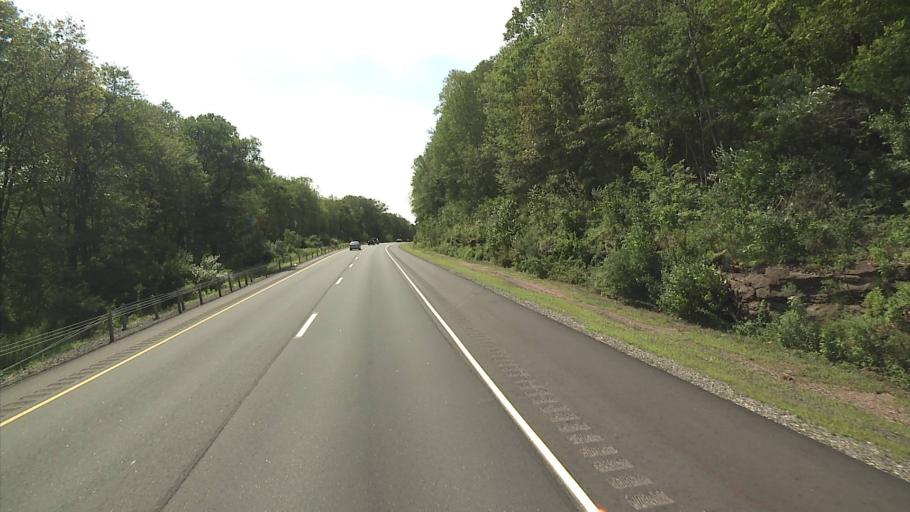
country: US
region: Connecticut
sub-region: Hartford County
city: Terramuggus
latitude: 41.6182
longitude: -72.4371
